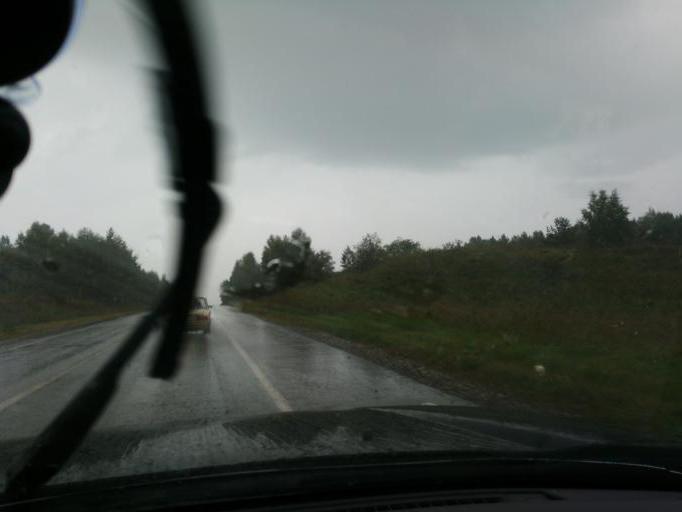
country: RU
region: Perm
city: Osa
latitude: 57.1505
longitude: 55.5293
